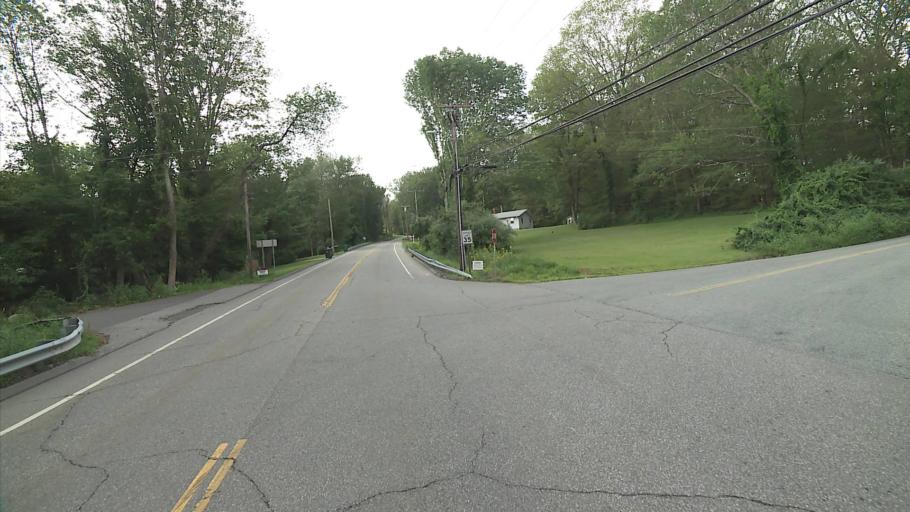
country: US
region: Connecticut
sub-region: New London County
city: Colchester
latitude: 41.5684
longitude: -72.4011
